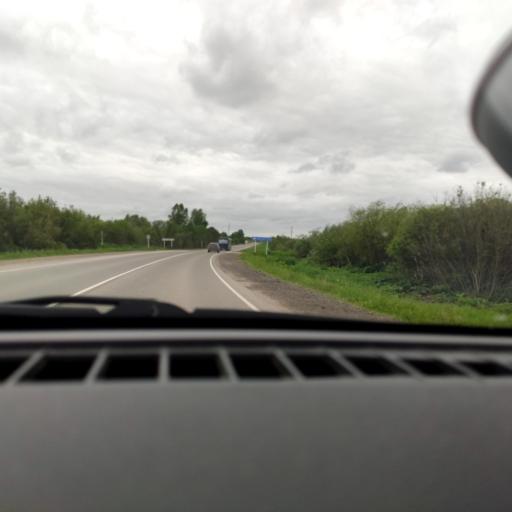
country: RU
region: Perm
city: Ust'-Kachka
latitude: 57.9388
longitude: 55.7570
